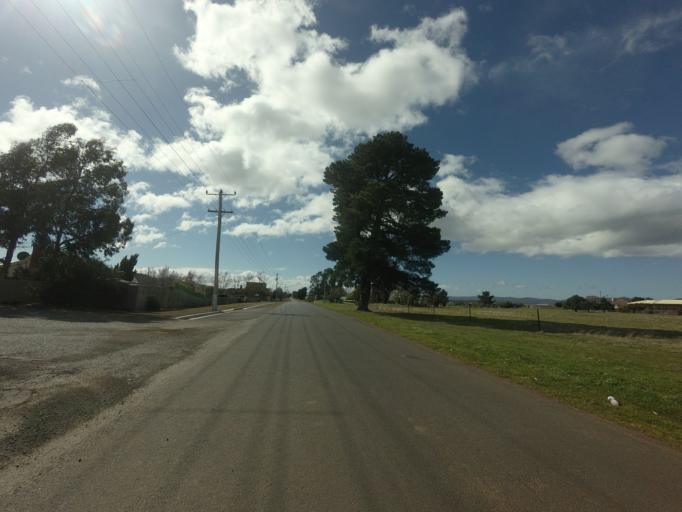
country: AU
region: Tasmania
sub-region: Northern Midlands
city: Evandale
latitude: -42.1425
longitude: 147.4217
